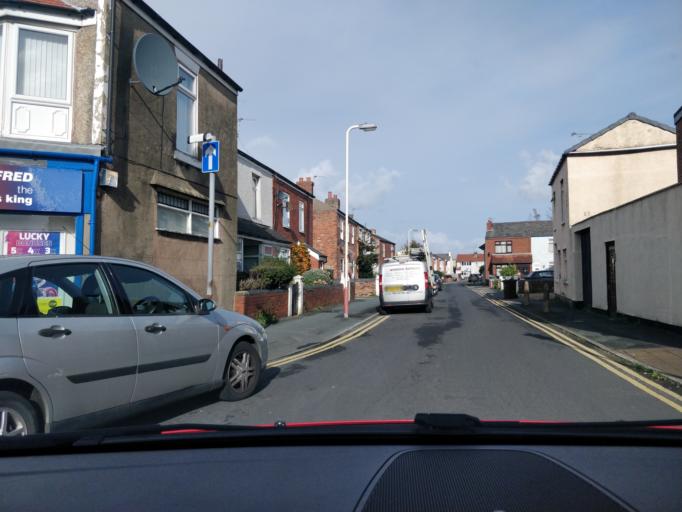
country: GB
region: England
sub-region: Sefton
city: Southport
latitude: 53.6365
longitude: -3.0088
